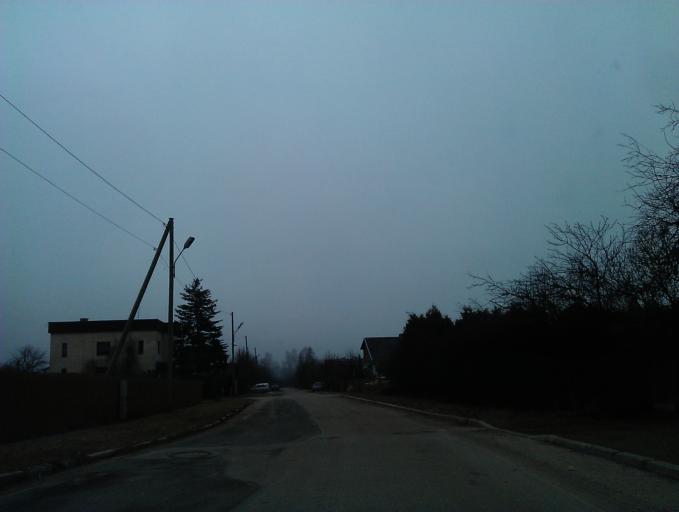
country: LV
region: Adazi
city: Adazi
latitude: 57.0720
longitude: 24.3241
